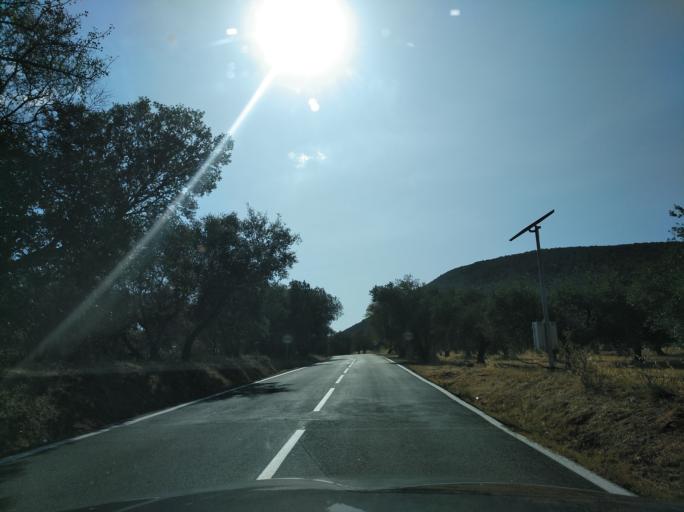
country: ES
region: Andalusia
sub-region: Provincia de Huelva
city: Rosal de la Frontera
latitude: 37.9598
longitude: -7.2538
